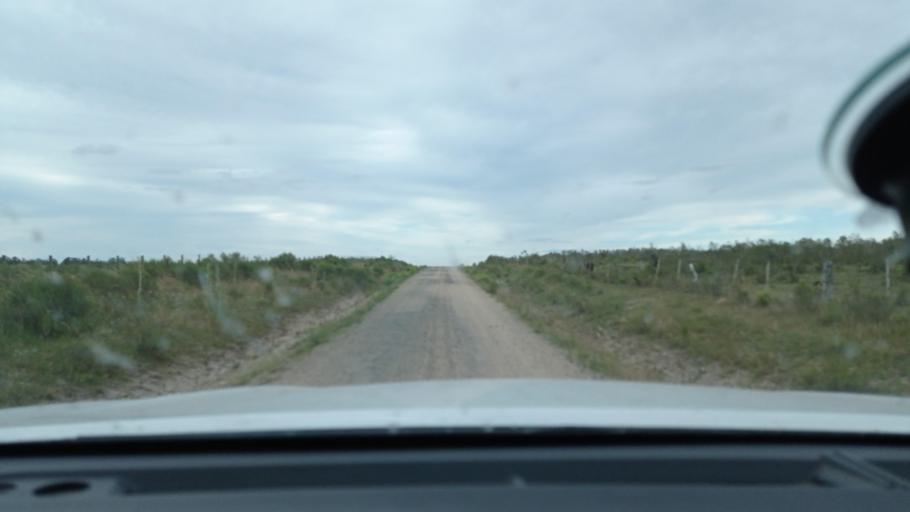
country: UY
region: Florida
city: Casupa
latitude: -34.1418
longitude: -55.7873
